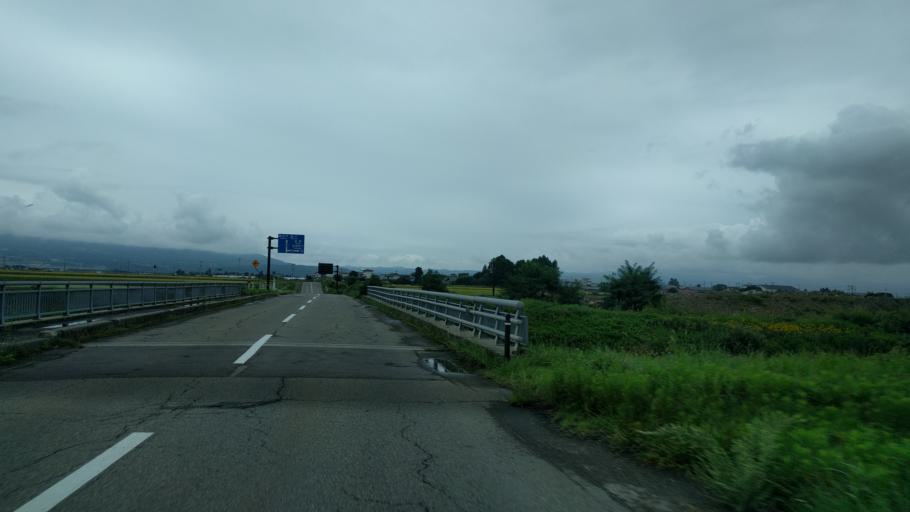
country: JP
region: Fukushima
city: Kitakata
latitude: 37.6142
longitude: 139.8515
